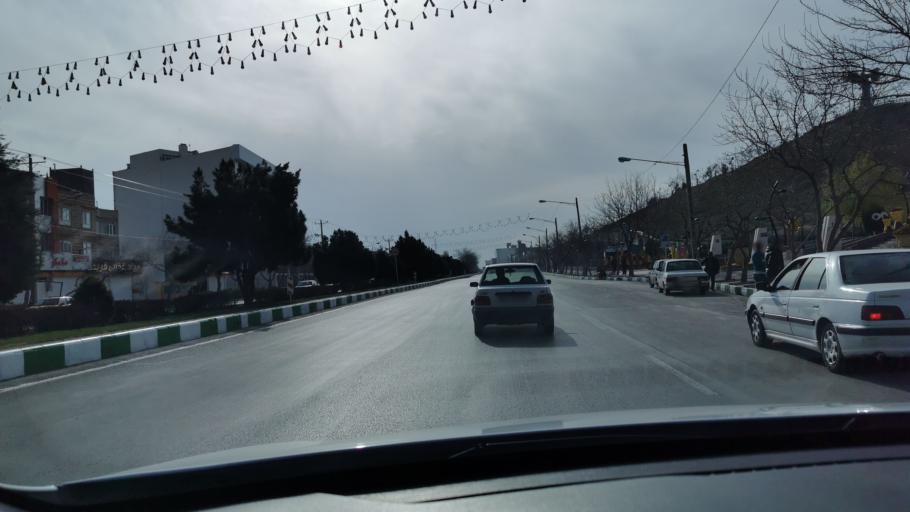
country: IR
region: Razavi Khorasan
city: Mashhad
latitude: 36.2957
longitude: 59.5297
